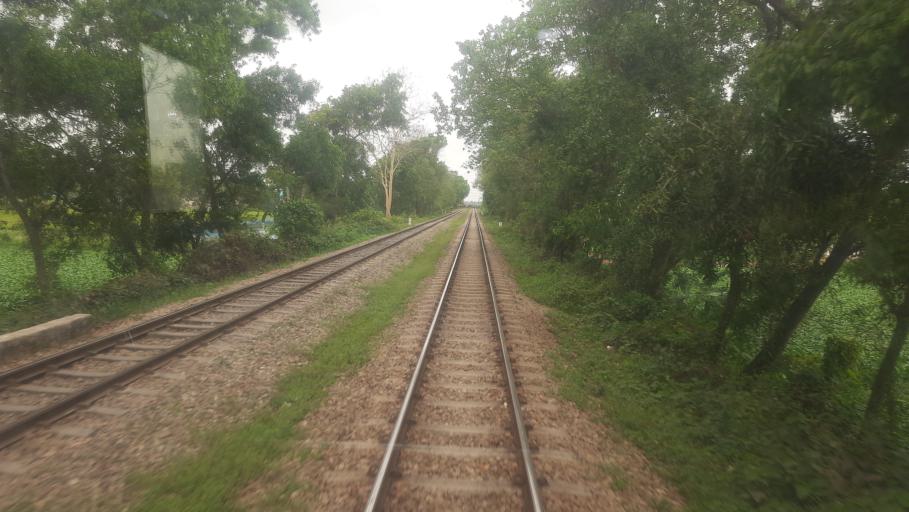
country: BD
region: Dhaka
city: Bhairab Bazar
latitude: 23.9664
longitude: 91.0998
